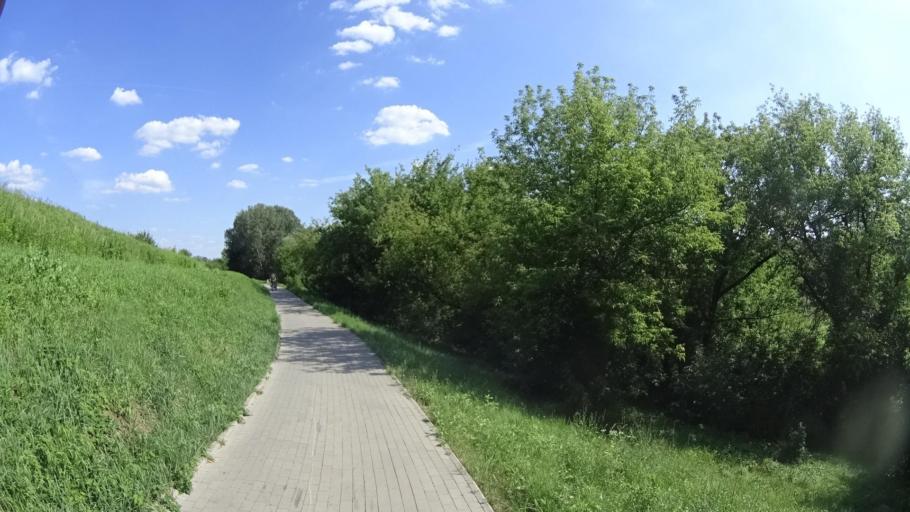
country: PL
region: Masovian Voivodeship
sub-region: Warszawa
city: Bialoleka
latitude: 52.3071
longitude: 20.9566
